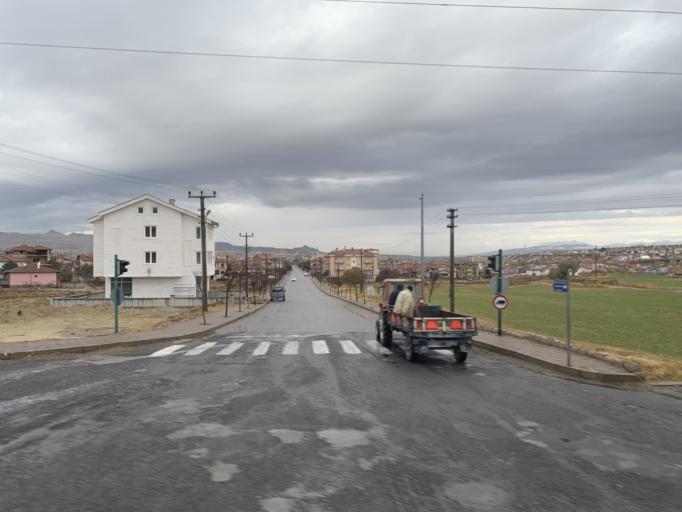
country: TR
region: Nevsehir
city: Avanos
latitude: 38.7120
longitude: 34.8582
